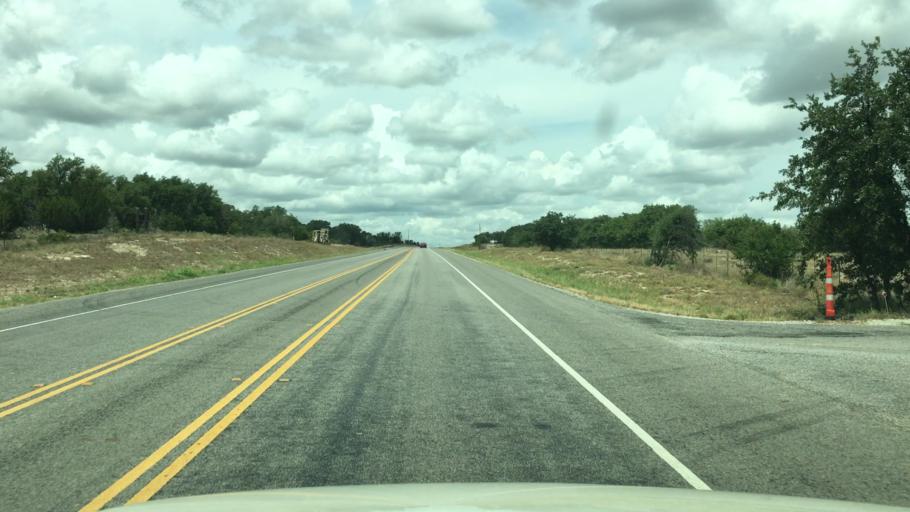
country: US
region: Texas
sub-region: McCulloch County
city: Brady
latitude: 31.0315
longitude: -99.2310
